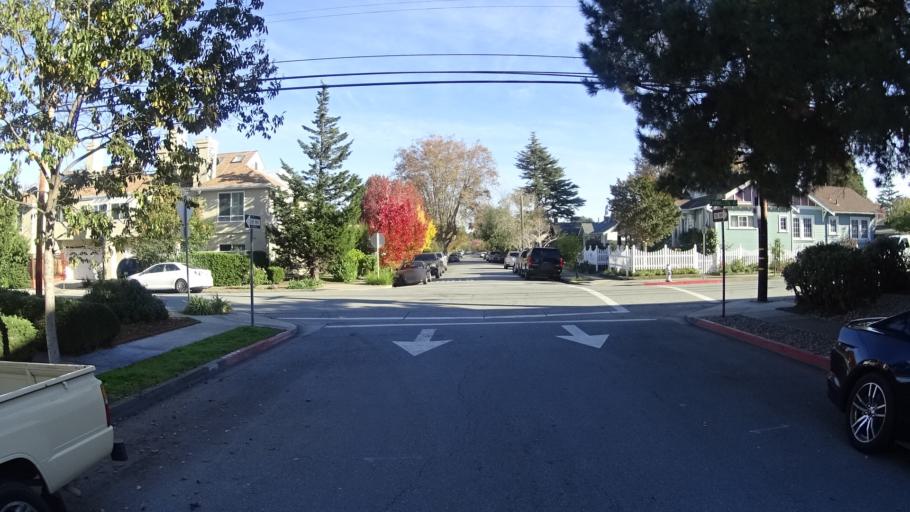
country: US
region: California
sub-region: San Mateo County
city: Burlingame
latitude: 37.5854
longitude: -122.3627
